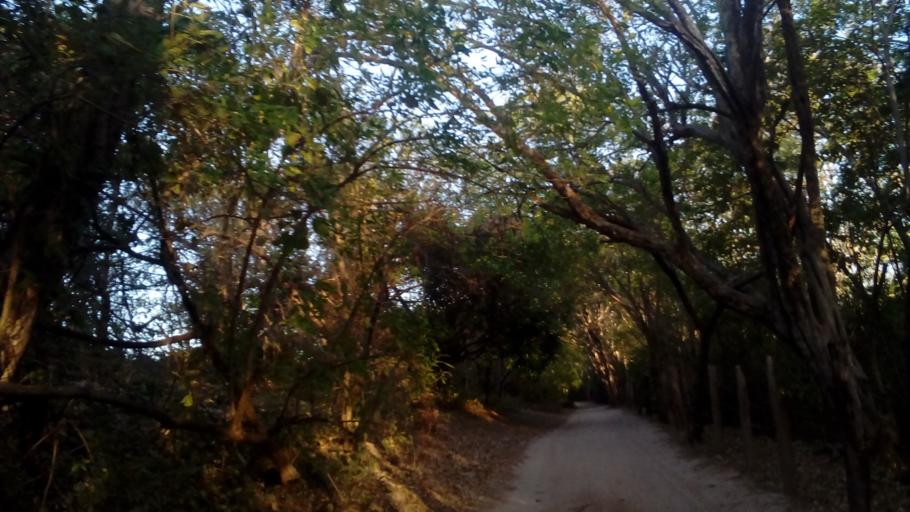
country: CR
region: Guanacaste
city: Sardinal
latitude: 10.3993
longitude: -85.8151
